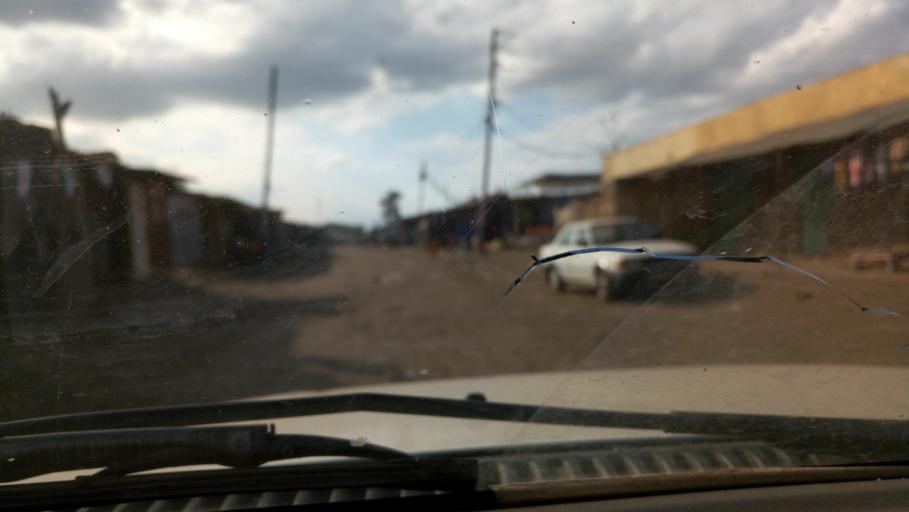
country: KE
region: Nairobi Area
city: Pumwani
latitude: -1.2504
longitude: 36.9116
